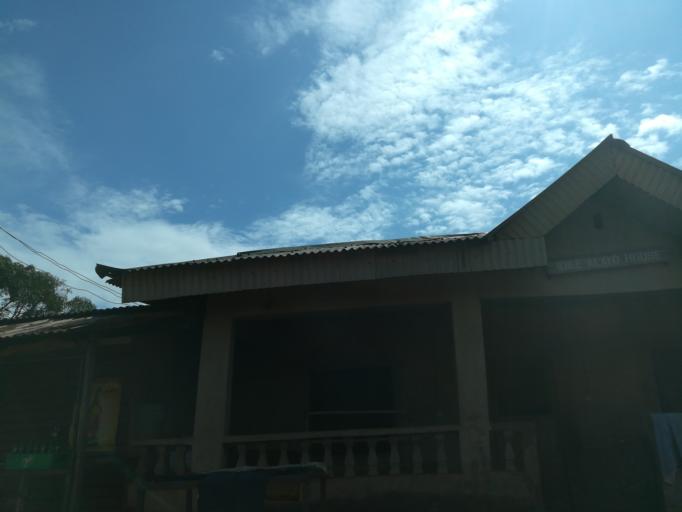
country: NG
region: Lagos
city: Ikorodu
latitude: 6.5940
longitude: 3.5211
